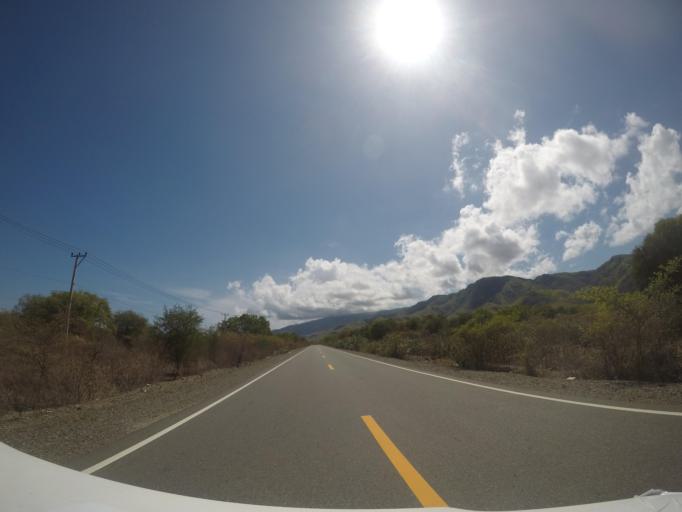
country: ID
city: Metinaro
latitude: -8.5104
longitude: 125.7926
